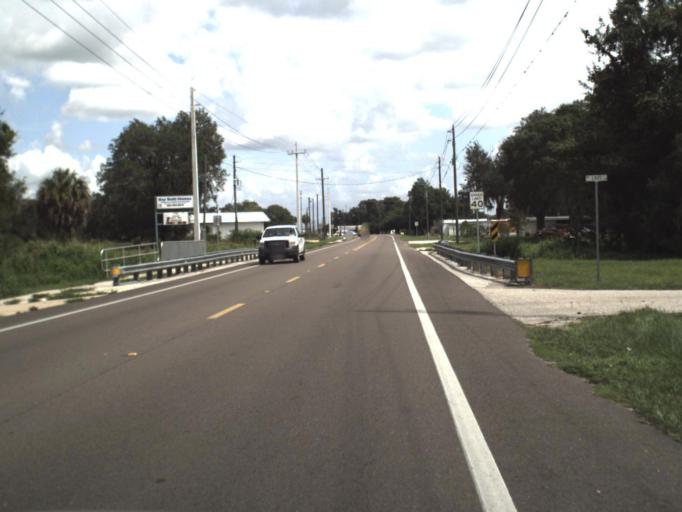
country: US
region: Florida
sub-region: DeSoto County
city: Arcadia
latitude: 27.2010
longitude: -81.8636
